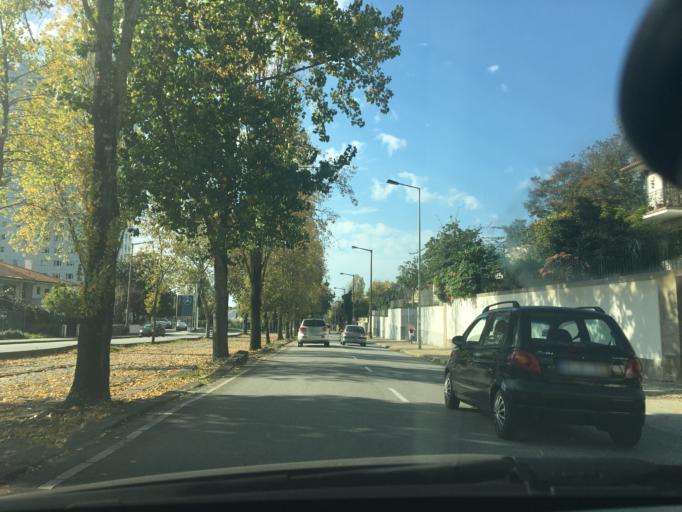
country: PT
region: Porto
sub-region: Matosinhos
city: Senhora da Hora
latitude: 41.1642
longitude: -8.6660
